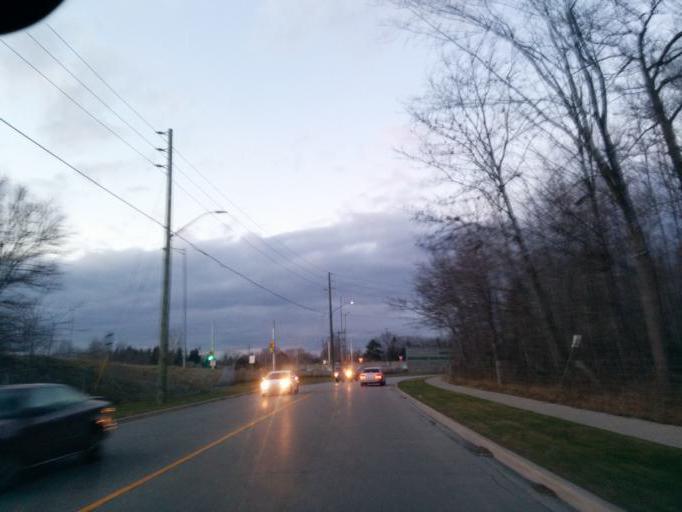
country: CA
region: Ontario
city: Etobicoke
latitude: 43.5829
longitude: -79.5815
